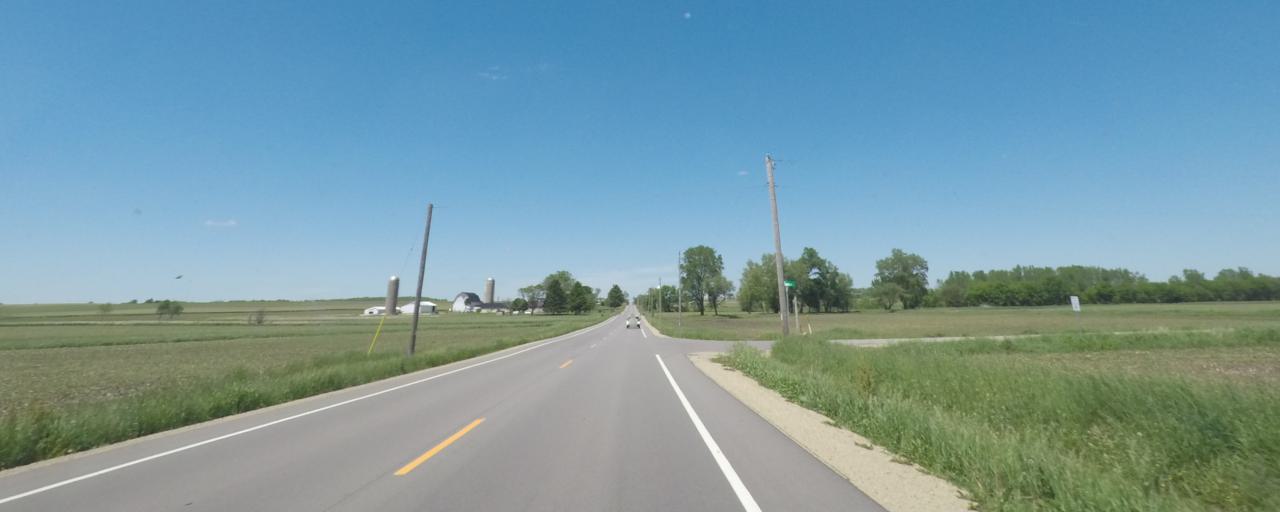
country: US
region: Wisconsin
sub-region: Green County
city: Brooklyn
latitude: 42.8011
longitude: -89.3692
